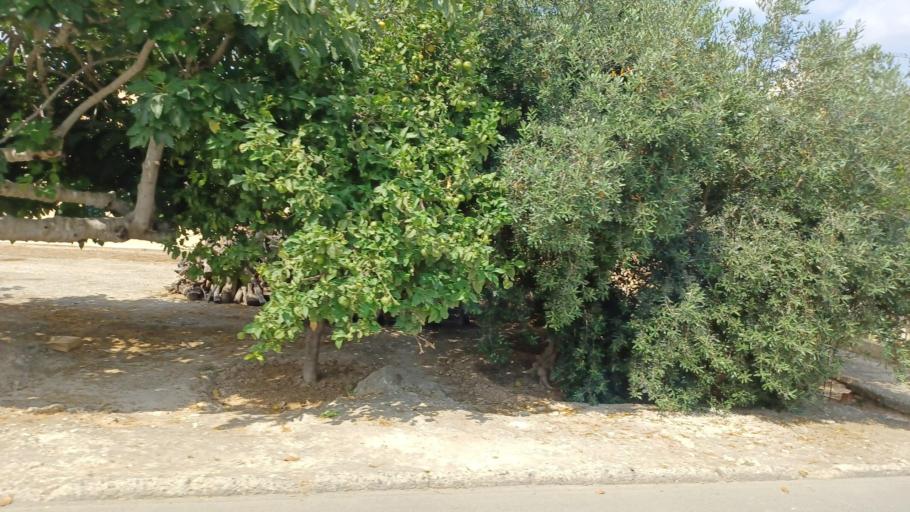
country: CY
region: Ammochostos
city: Deryneia
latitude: 35.0605
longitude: 33.9669
